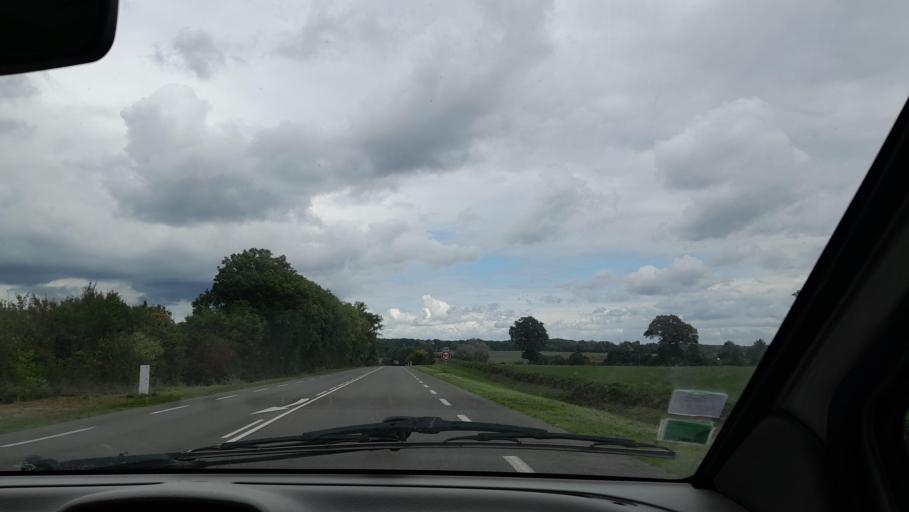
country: FR
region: Pays de la Loire
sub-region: Departement de la Mayenne
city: Montigne-le-Brillant
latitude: 48.0036
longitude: -0.8392
